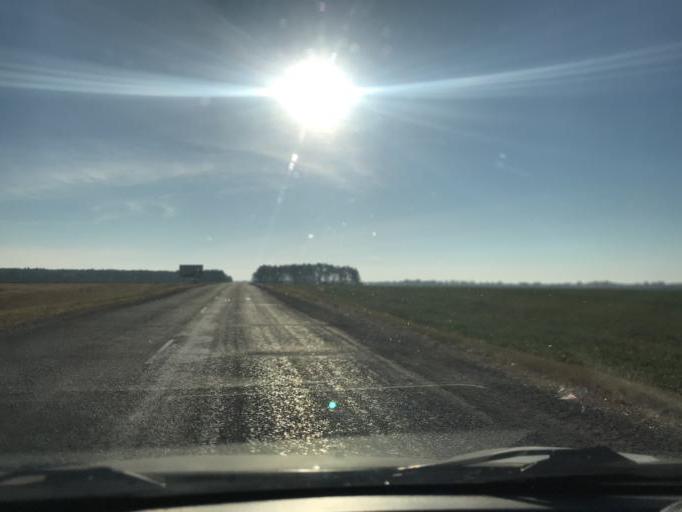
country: BY
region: Gomel
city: Khoyniki
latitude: 51.8176
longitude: 30.0881
